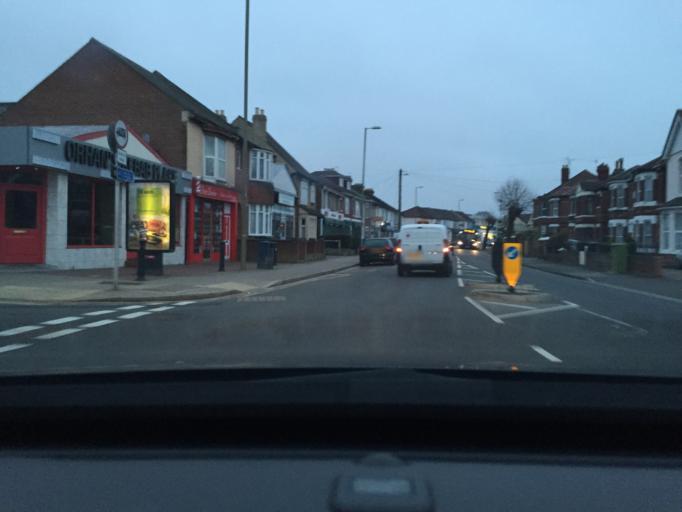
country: GB
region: England
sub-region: Hampshire
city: Gosport
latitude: 50.8041
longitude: -1.1507
